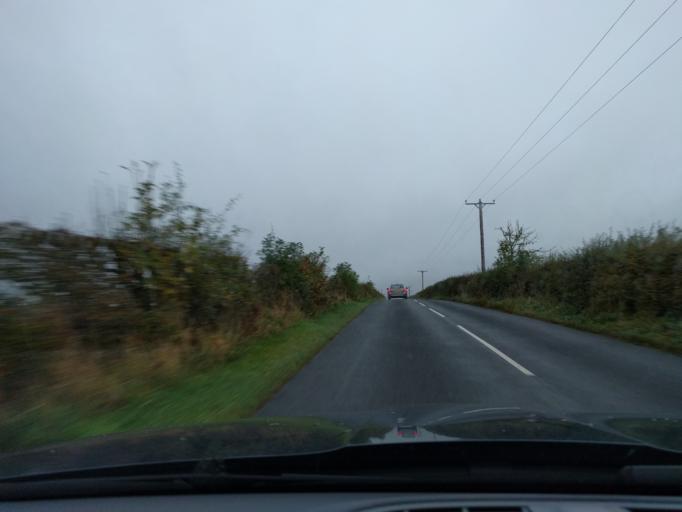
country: GB
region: England
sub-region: Northumberland
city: Ford
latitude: 55.7297
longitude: -2.1086
